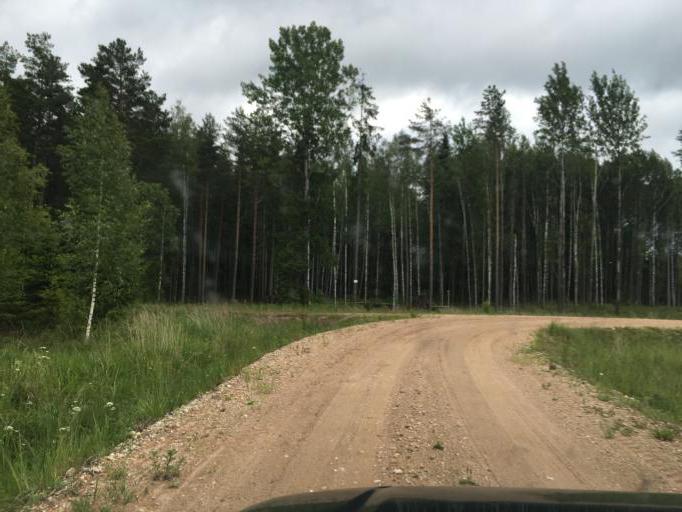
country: LV
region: Vilaka
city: Vilaka
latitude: 57.3882
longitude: 27.4953
